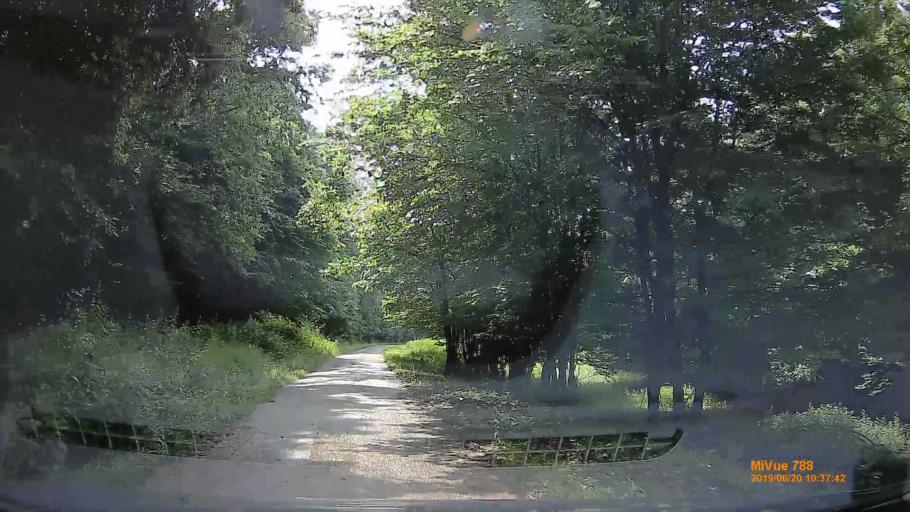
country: HU
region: Baranya
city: Hidas
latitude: 46.2035
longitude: 18.5340
